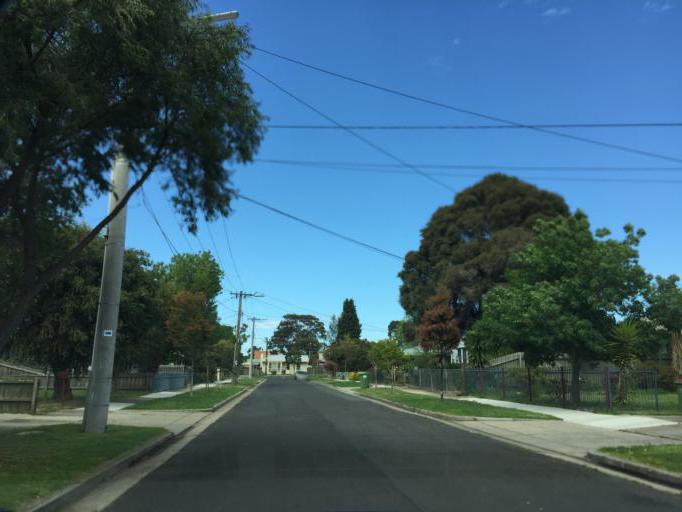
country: AU
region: Victoria
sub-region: Maribyrnong
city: Braybrook
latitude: -37.7845
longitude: 144.8626
